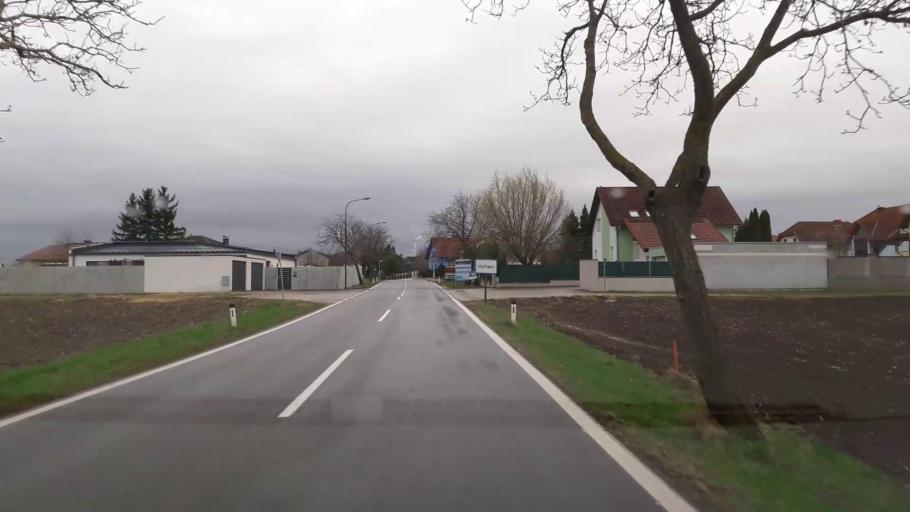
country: AT
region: Lower Austria
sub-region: Politischer Bezirk Bruck an der Leitha
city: Scharndorf
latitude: 48.0714
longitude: 16.7919
